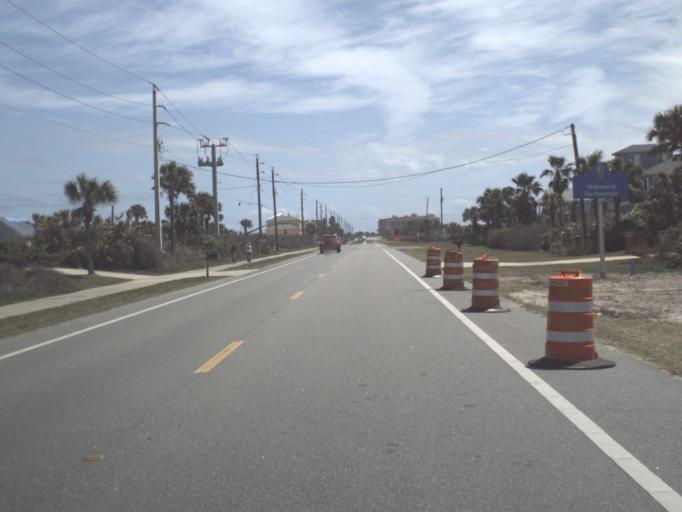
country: US
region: Florida
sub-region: Flagler County
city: Palm Coast
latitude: 29.6616
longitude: -81.2103
